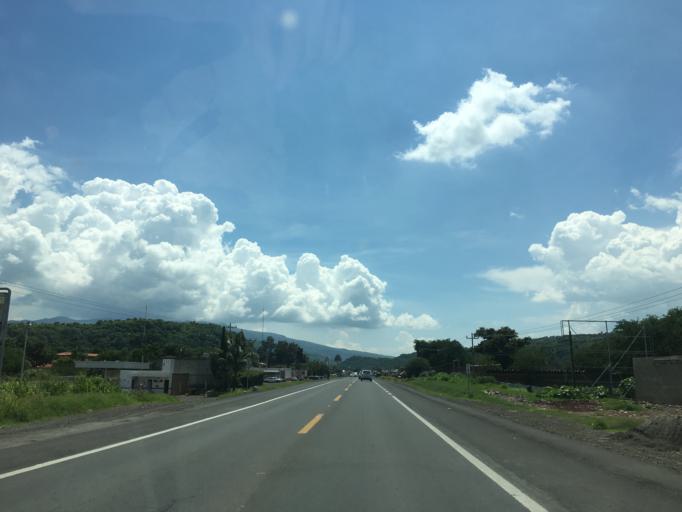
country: MX
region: Nayarit
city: Ixtlan del Rio
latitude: 21.0370
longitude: -104.3953
